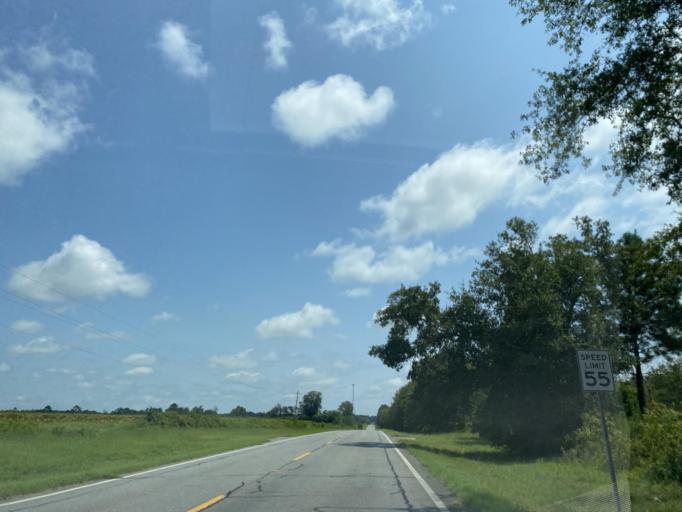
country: US
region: Georgia
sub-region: Wilcox County
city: Abbeville
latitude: 31.9959
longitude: -83.1852
